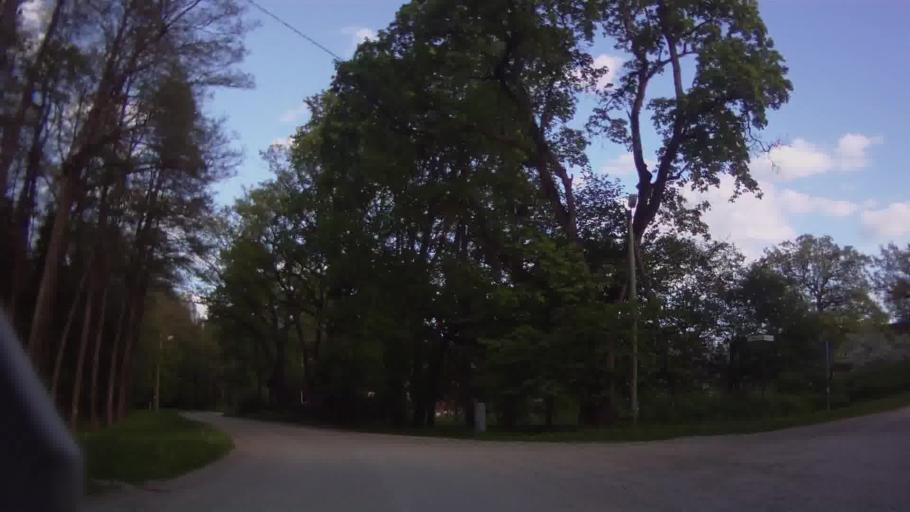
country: LV
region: Baldone
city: Baldone
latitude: 56.7426
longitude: 24.4057
